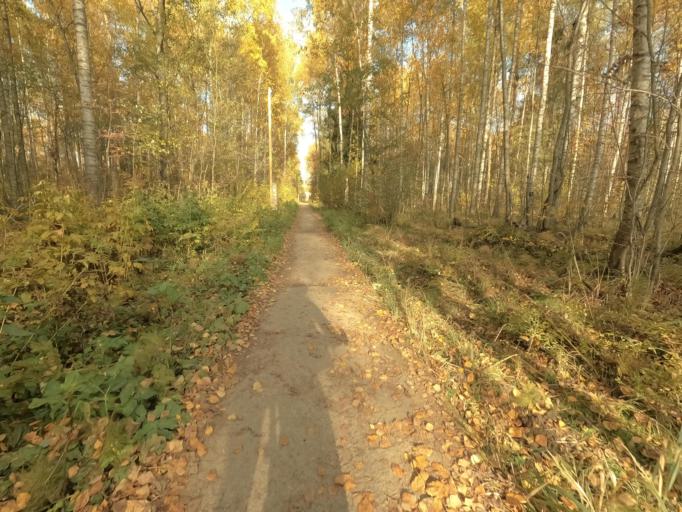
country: RU
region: Leningrad
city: Mga
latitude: 59.7608
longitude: 31.1149
